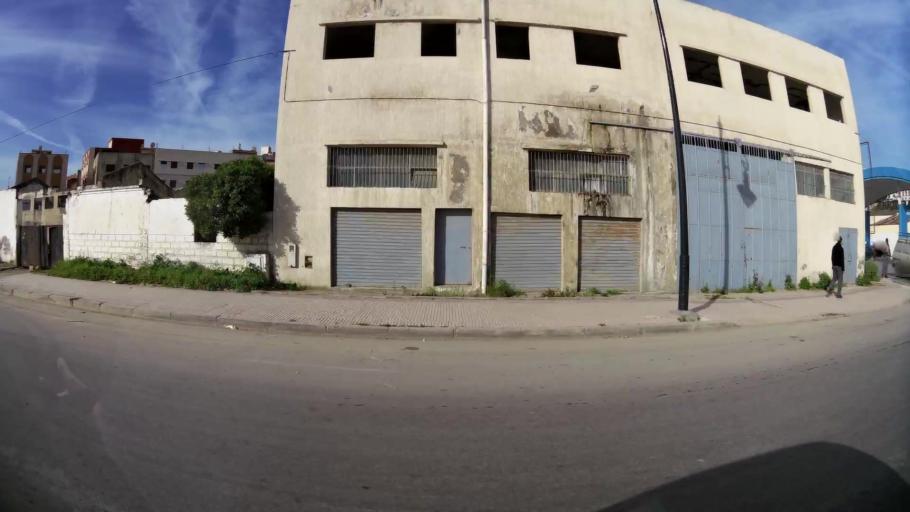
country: MA
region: Tanger-Tetouan
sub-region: Tanger-Assilah
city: Tangier
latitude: 35.7650
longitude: -5.7836
